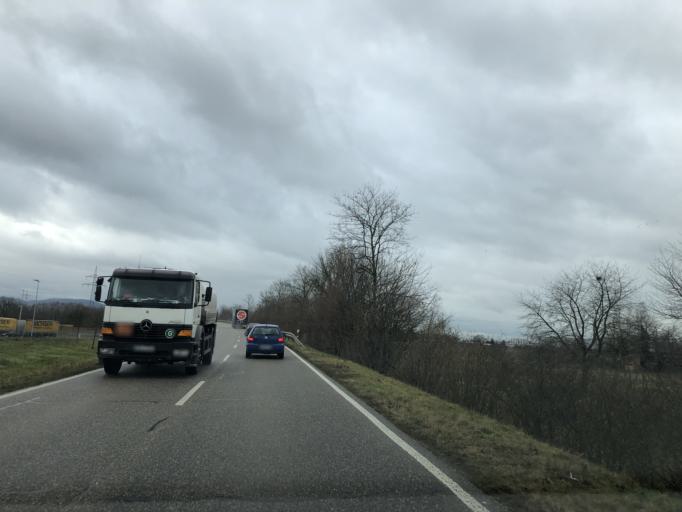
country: DE
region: Baden-Wuerttemberg
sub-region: Karlsruhe Region
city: Muggensturm
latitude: 48.8857
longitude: 8.2987
